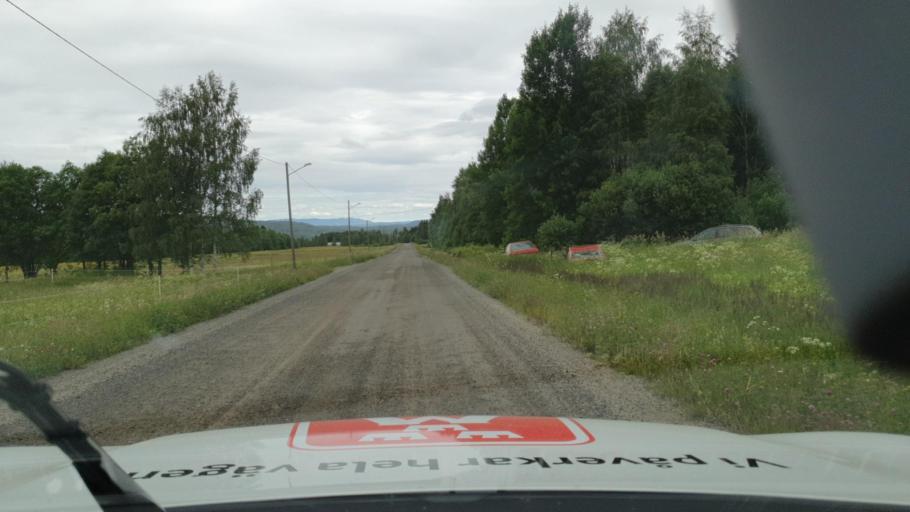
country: SE
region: Vaesterbotten
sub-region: Bjurholms Kommun
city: Bjurholm
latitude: 63.7842
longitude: 19.3777
